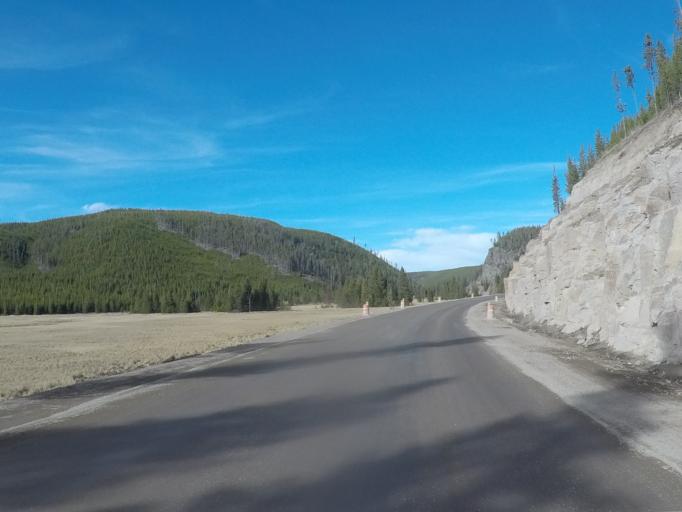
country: US
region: Montana
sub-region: Gallatin County
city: West Yellowstone
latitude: 44.8155
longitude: -110.7296
